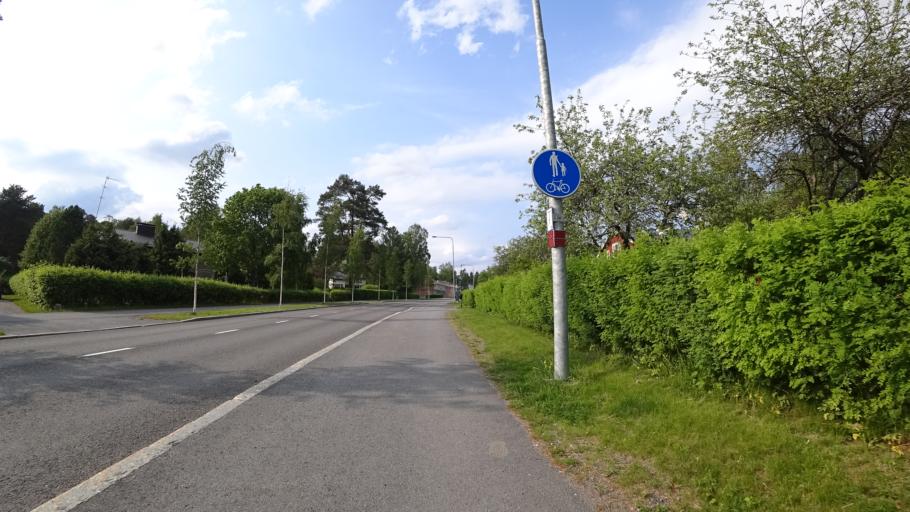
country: FI
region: Pirkanmaa
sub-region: Tampere
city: Pirkkala
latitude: 61.4996
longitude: 23.6289
